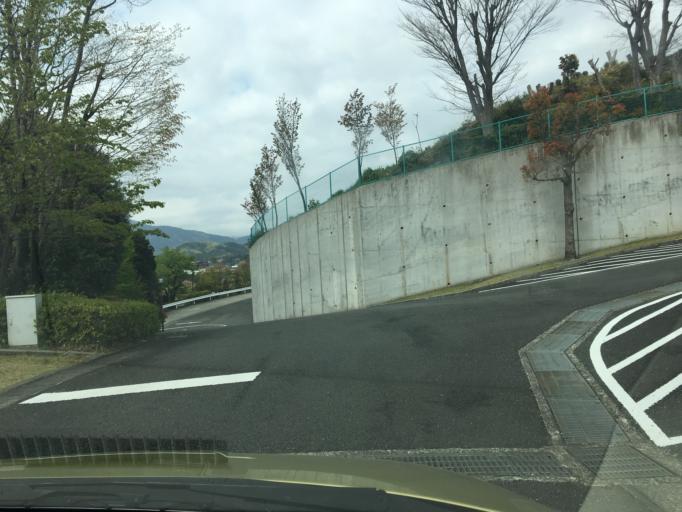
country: JP
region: Kanagawa
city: Zama
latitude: 35.5360
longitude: 139.3173
